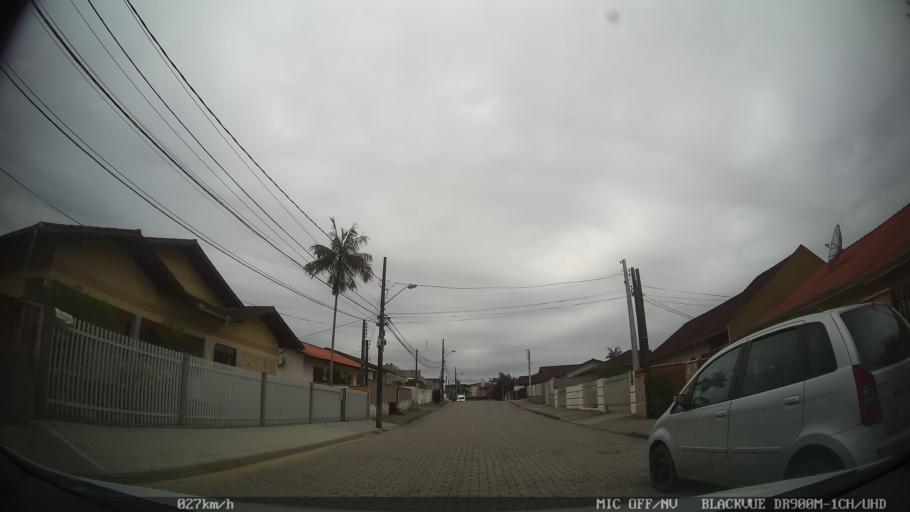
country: BR
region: Santa Catarina
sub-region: Joinville
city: Joinville
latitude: -26.2725
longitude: -48.8825
